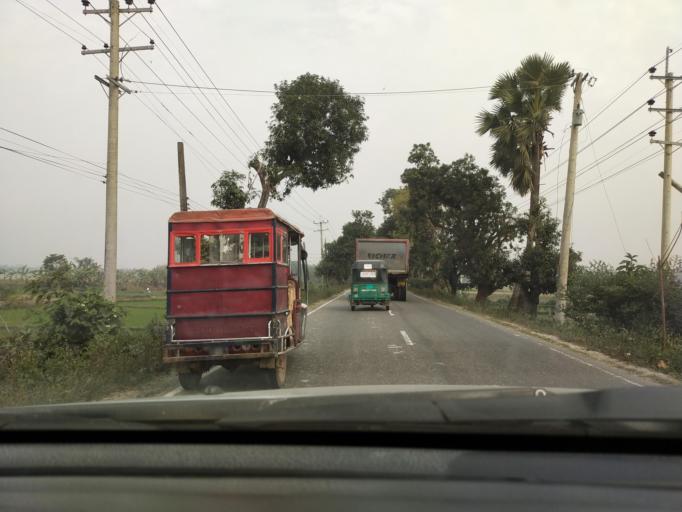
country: BD
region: Dhaka
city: Narsingdi
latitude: 24.0167
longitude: 90.7374
